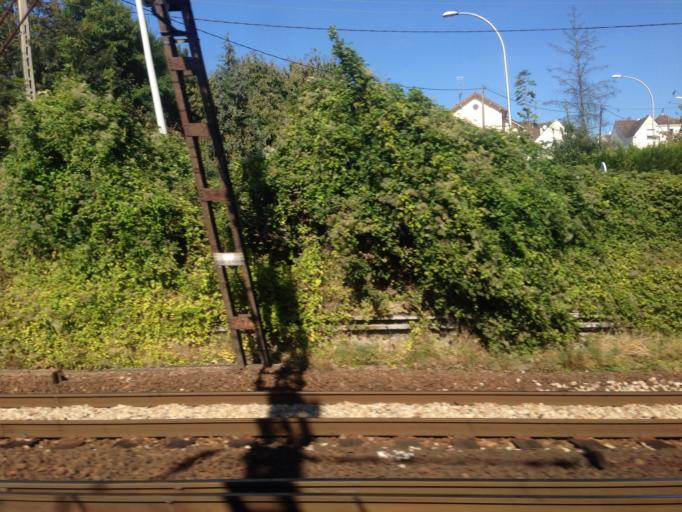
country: FR
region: Ile-de-France
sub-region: Departement de l'Essonne
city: Savigny-sur-Orge
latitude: 48.6803
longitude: 2.3616
